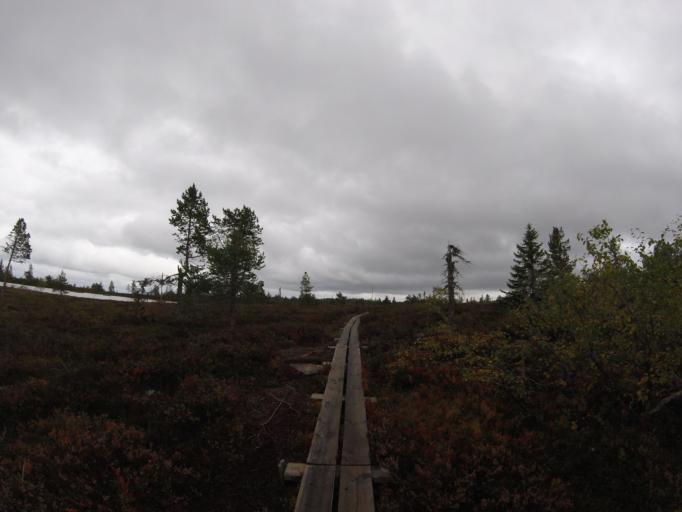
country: NO
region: Buskerud
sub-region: Flesberg
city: Lampeland
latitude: 59.7736
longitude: 9.4062
